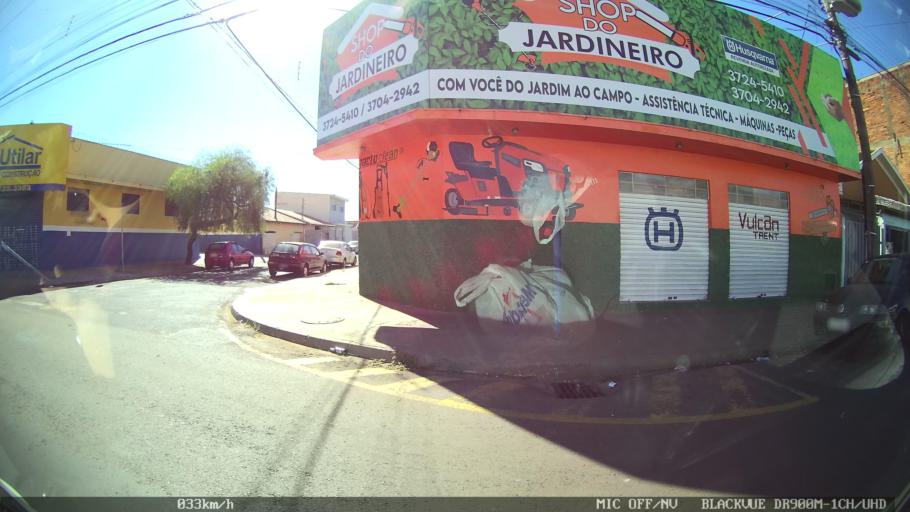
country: BR
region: Sao Paulo
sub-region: Franca
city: Franca
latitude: -20.5345
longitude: -47.3652
